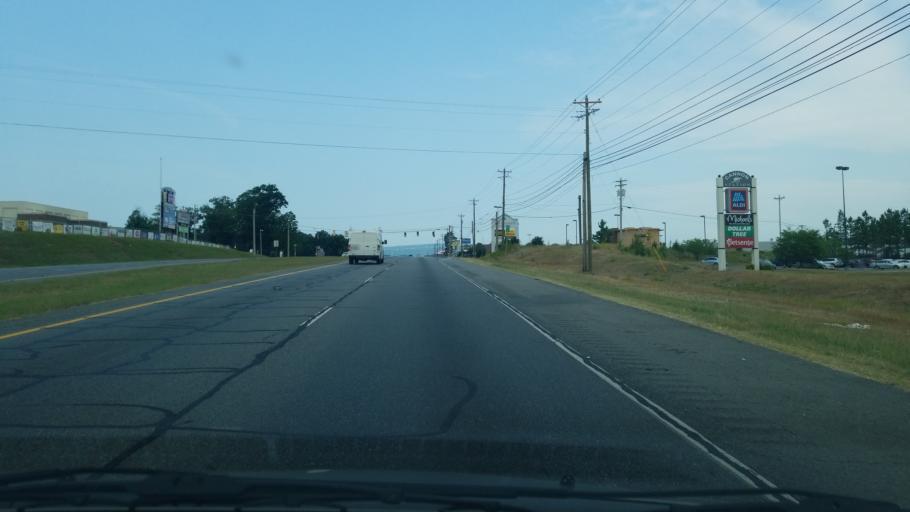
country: US
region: Georgia
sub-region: Catoosa County
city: Fort Oglethorpe
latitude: 34.9469
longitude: -85.2317
